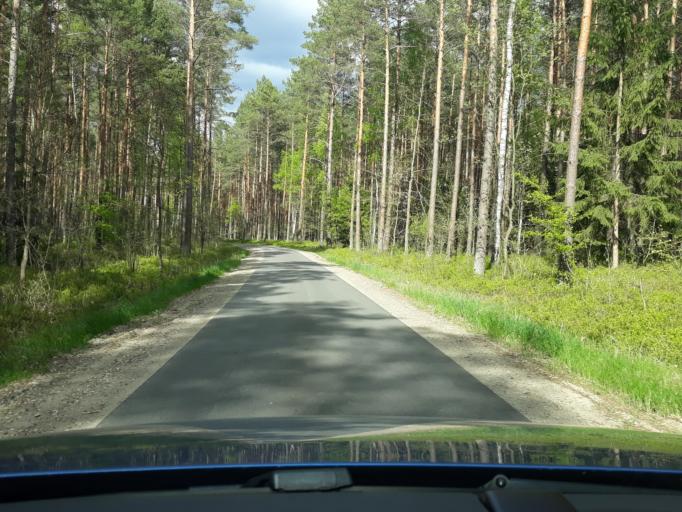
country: PL
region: Pomeranian Voivodeship
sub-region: Powiat czluchowski
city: Czluchow
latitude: 53.7273
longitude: 17.3412
